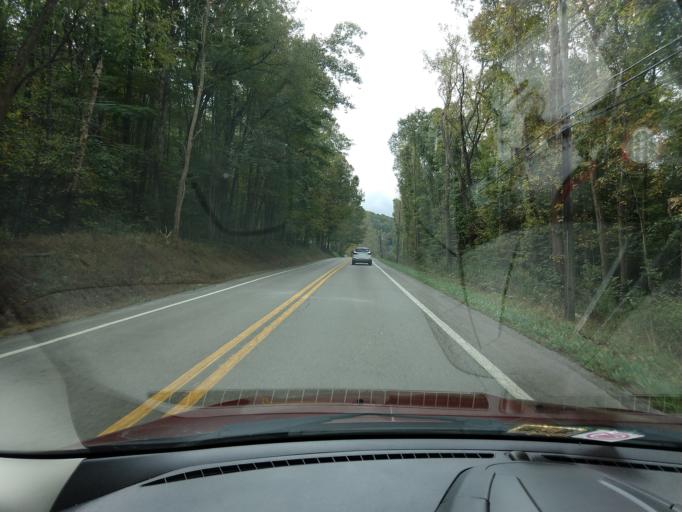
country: US
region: West Virginia
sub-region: Barbour County
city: Belington
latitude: 38.9877
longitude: -79.9390
